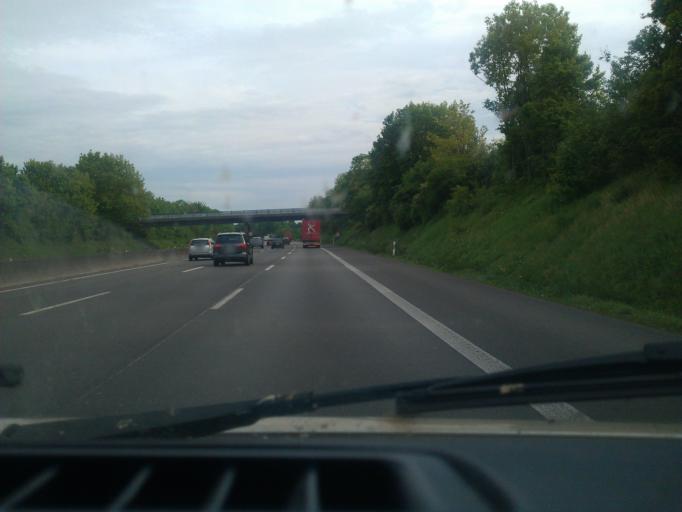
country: DE
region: North Rhine-Westphalia
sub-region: Regierungsbezirk Koln
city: Titz
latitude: 51.0766
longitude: 6.4258
